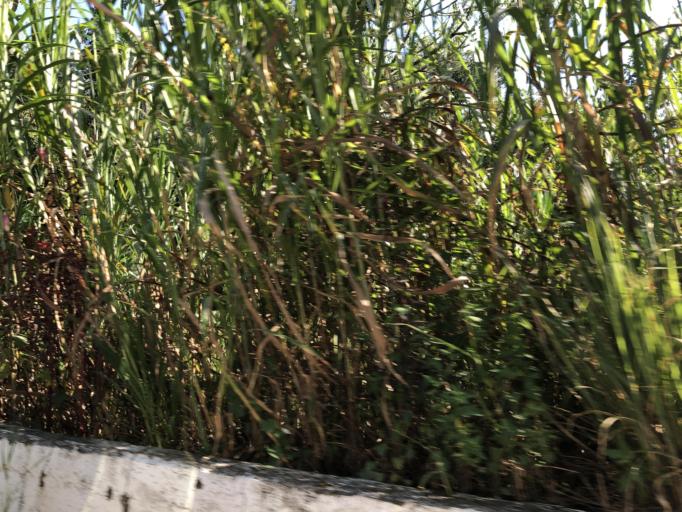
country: TW
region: Taiwan
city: Yujing
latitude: 23.0535
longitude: 120.3785
